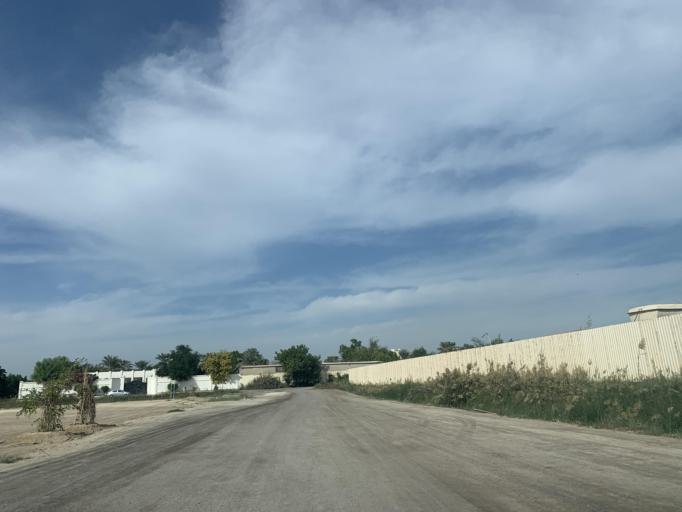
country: BH
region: Central Governorate
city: Madinat Hamad
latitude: 26.1191
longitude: 50.4698
